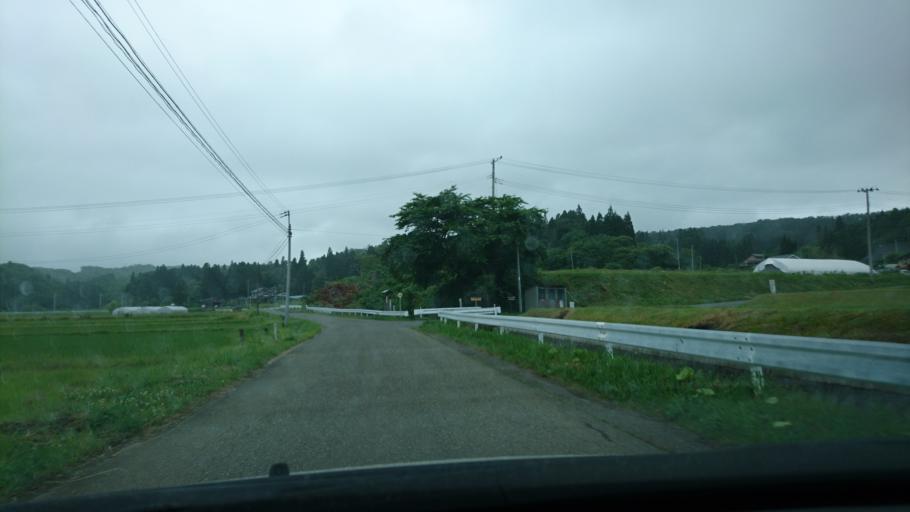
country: JP
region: Iwate
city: Ichinoseki
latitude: 38.9512
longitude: 141.0477
